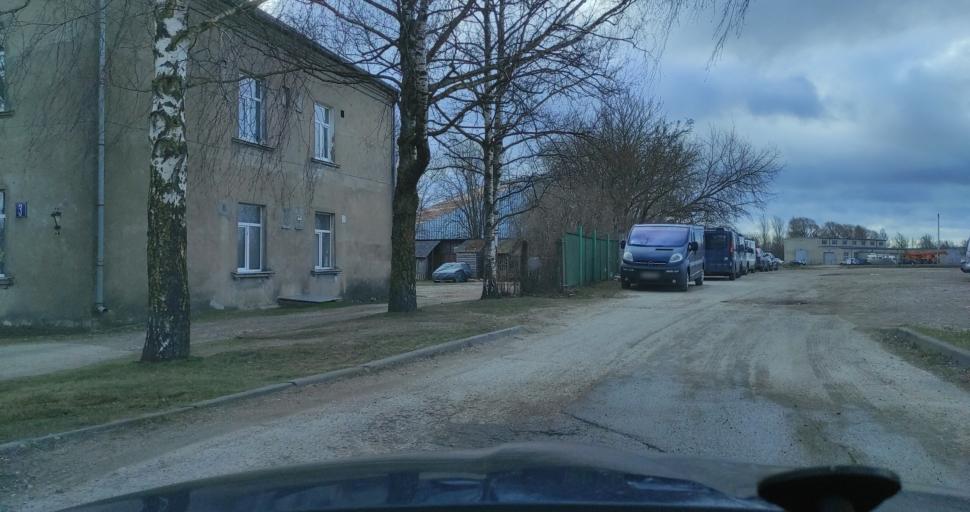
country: LV
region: Ventspils
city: Ventspils
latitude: 57.3867
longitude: 21.5810
